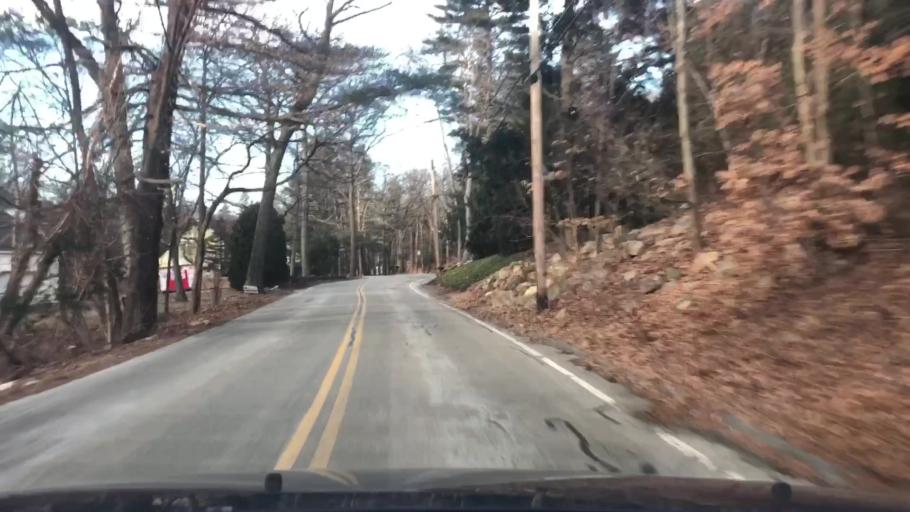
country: US
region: Massachusetts
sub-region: Essex County
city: Andover
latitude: 42.6692
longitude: -71.1104
